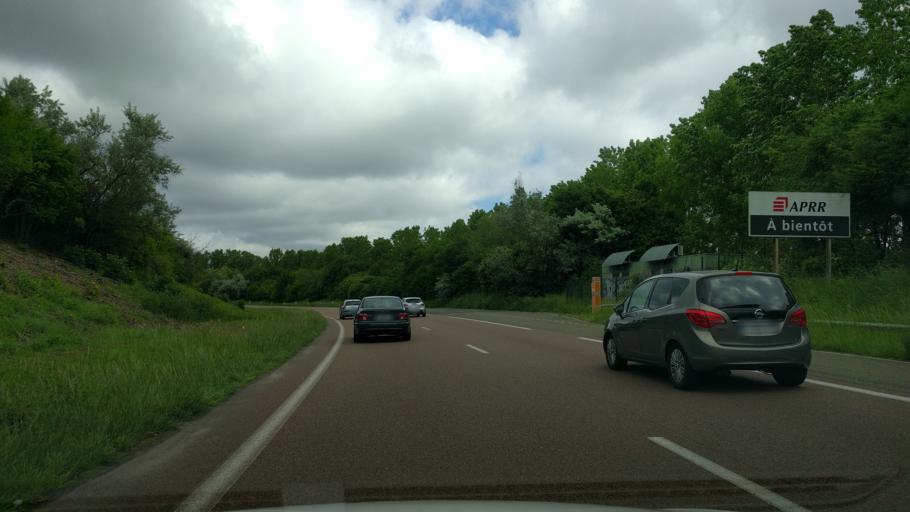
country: FR
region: Ile-de-France
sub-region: Departement de Seine-et-Marne
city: Lieusaint
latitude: 48.6311
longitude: 2.5381
